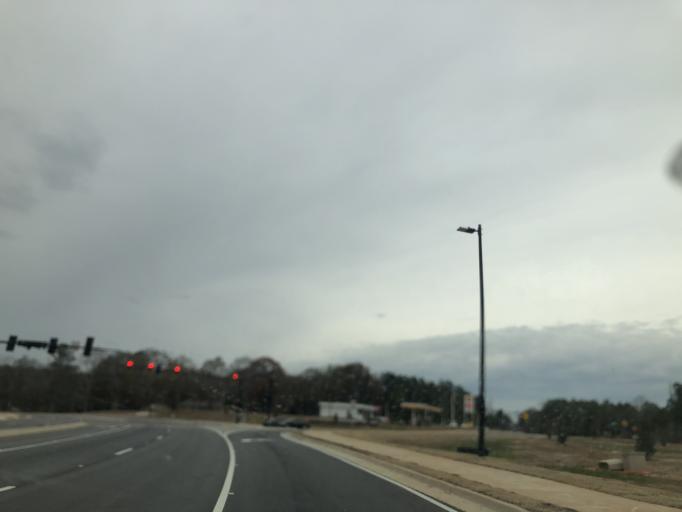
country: US
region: Georgia
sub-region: Clayton County
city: Conley
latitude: 33.6249
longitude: -84.2557
